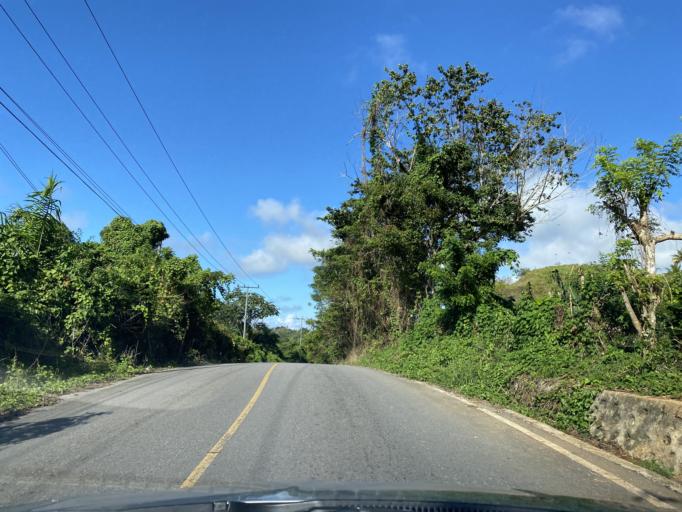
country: DO
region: Samana
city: Sanchez
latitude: 19.2485
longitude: -69.5938
